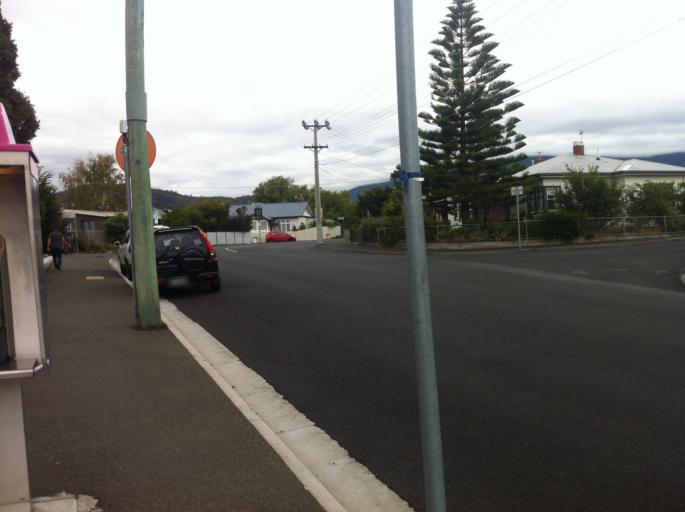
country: AU
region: Tasmania
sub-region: Hobart
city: New Town
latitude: -42.8518
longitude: 147.3058
